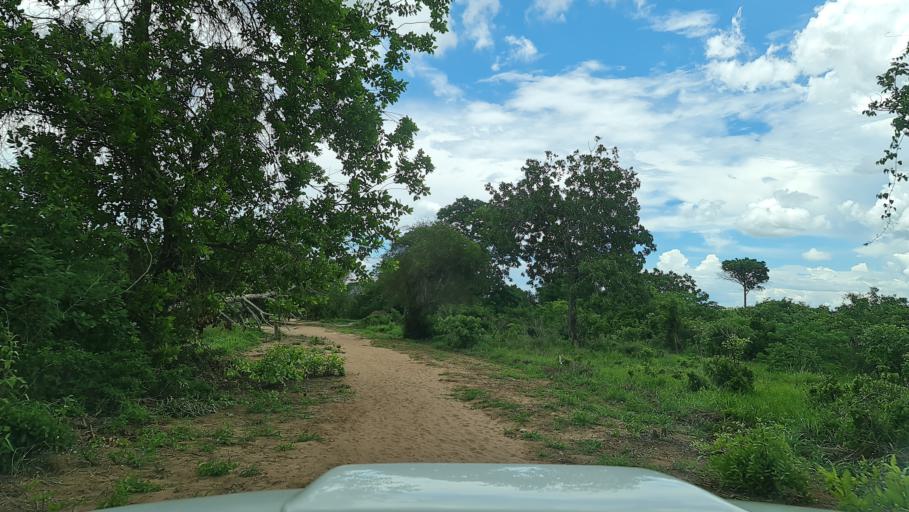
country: MZ
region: Nampula
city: Ilha de Mocambique
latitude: -15.4967
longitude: 40.1637
